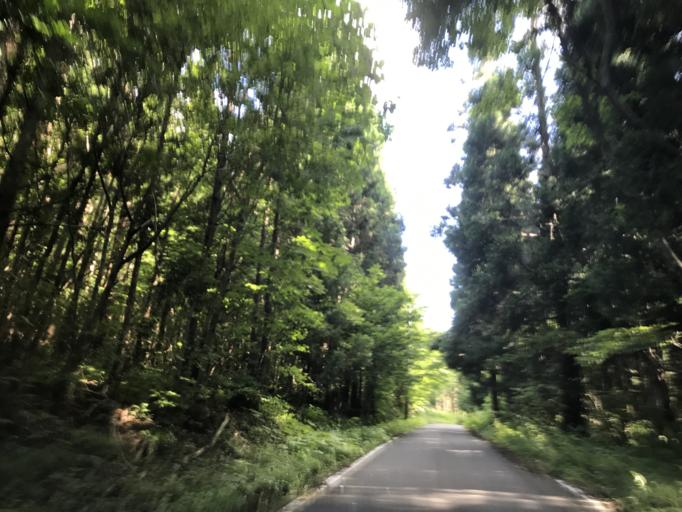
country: JP
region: Iwate
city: Ichinoseki
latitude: 38.8961
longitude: 140.9081
